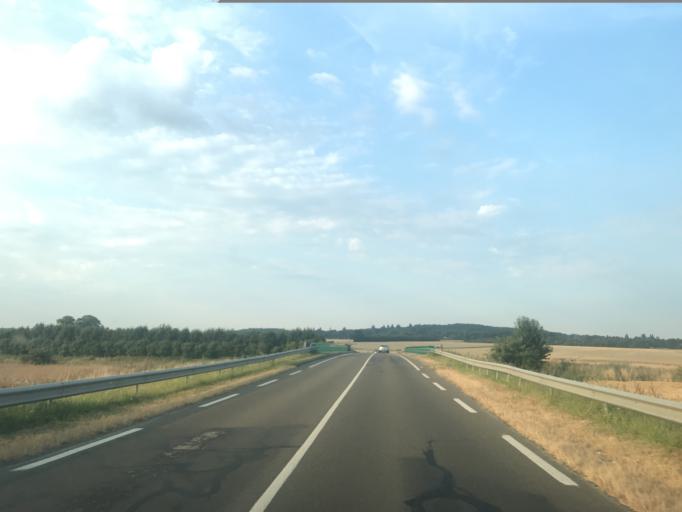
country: FR
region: Ile-de-France
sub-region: Departement des Yvelines
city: Villiers-Saint-Frederic
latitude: 48.7964
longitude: 1.8713
